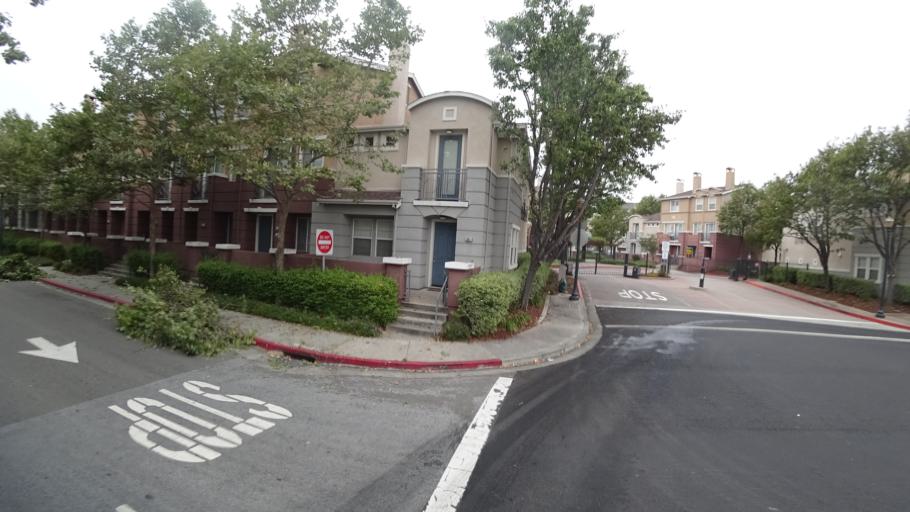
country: US
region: California
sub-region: Alameda County
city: Hayward
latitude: 37.6699
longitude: -122.0849
